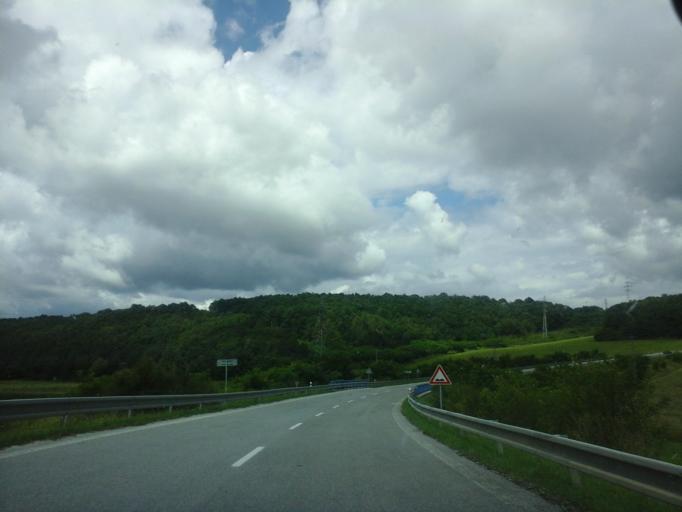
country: SK
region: Kosicky
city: Roznava
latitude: 48.5252
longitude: 20.4080
